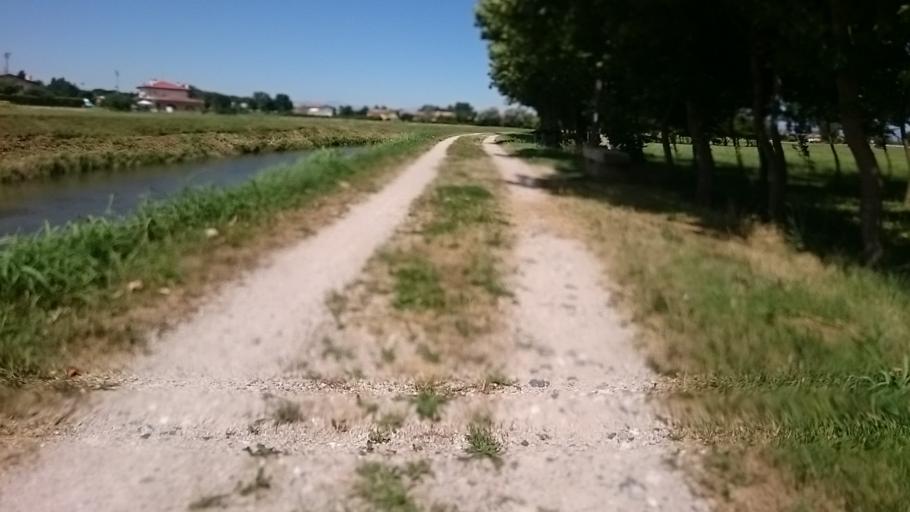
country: IT
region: Veneto
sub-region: Provincia di Padova
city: Codiverno
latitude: 45.4742
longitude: 11.9514
